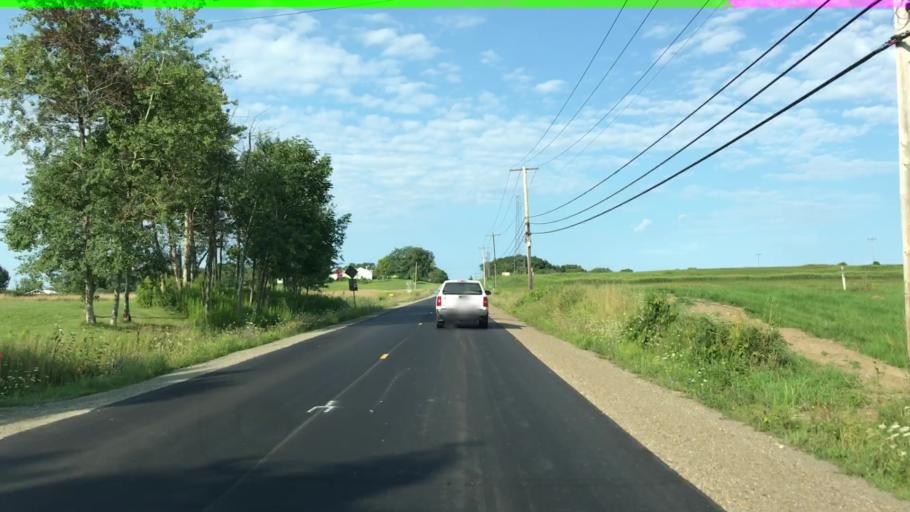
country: US
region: New York
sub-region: Chautauqua County
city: Fredonia
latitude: 42.3289
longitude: -79.3319
